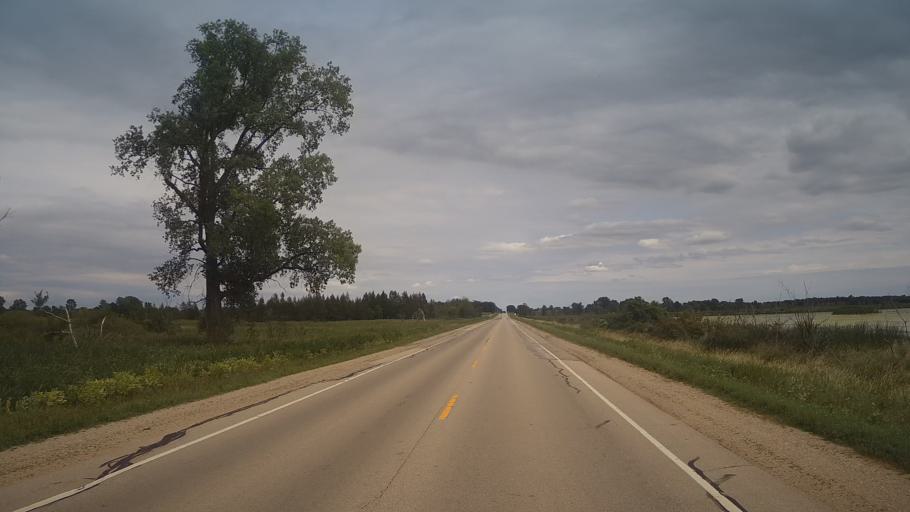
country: US
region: Wisconsin
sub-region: Green Lake County
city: Berlin
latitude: 44.0487
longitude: -88.9590
